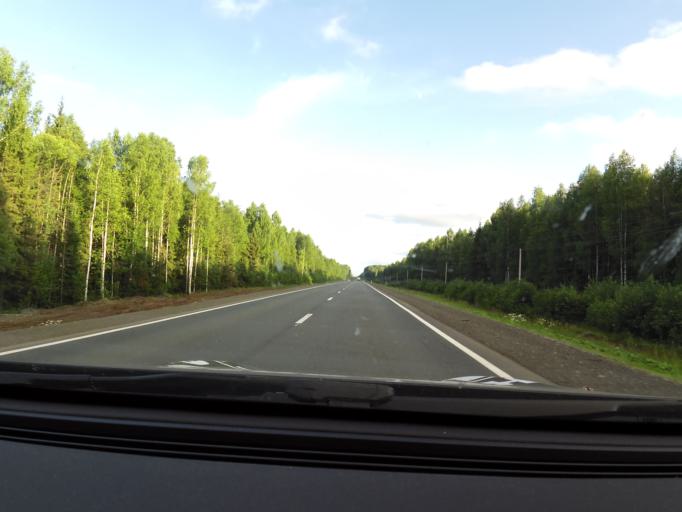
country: RU
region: Perm
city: Siva
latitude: 58.5867
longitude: 53.8821
